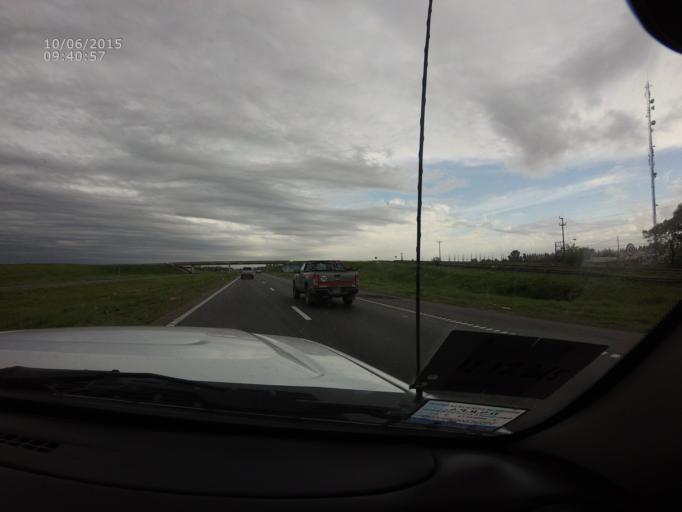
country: AR
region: Buenos Aires
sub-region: Partido de Zarate
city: Zarate
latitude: -34.0811
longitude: -59.2076
